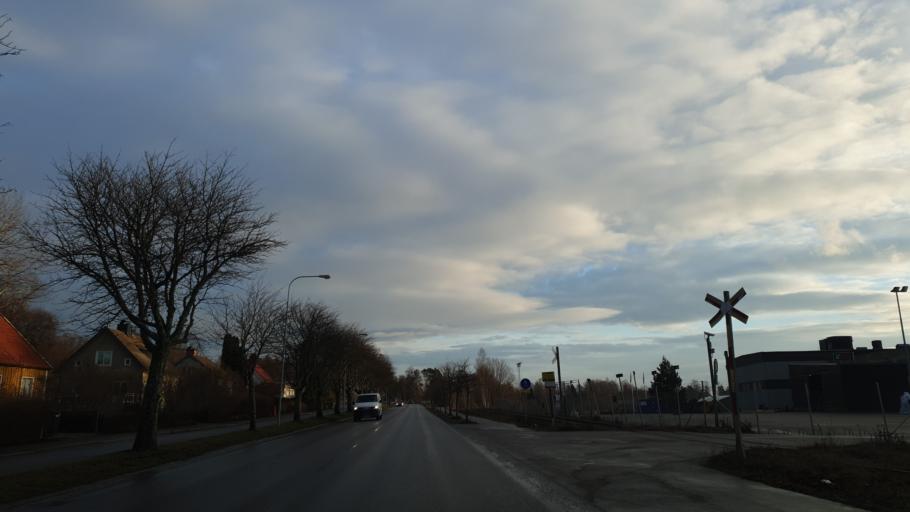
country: SE
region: Gaevleborg
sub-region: Hudiksvalls Kommun
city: Hudiksvall
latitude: 61.7245
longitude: 17.1357
